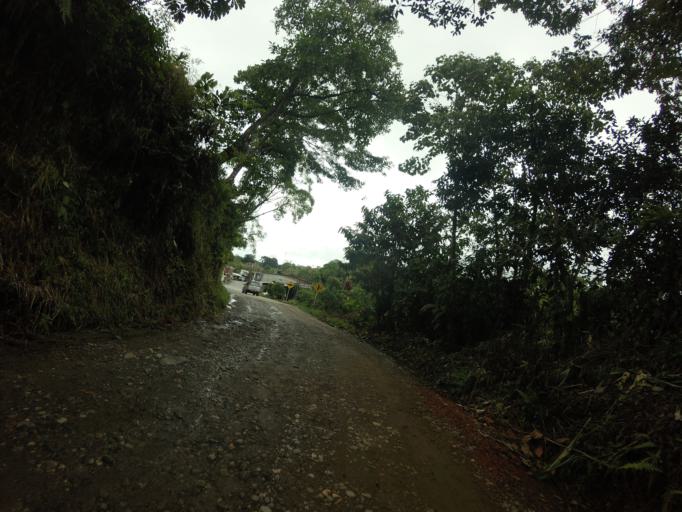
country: CO
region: Caldas
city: Victoria
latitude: 5.3228
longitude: -74.9411
